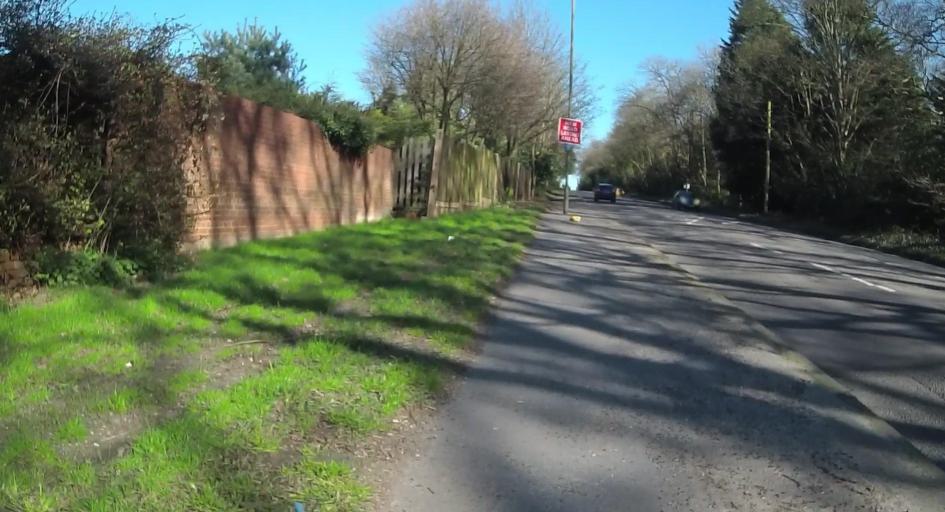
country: GB
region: England
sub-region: Royal Borough of Windsor and Maidenhead
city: Ascot
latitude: 51.4113
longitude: -0.6943
